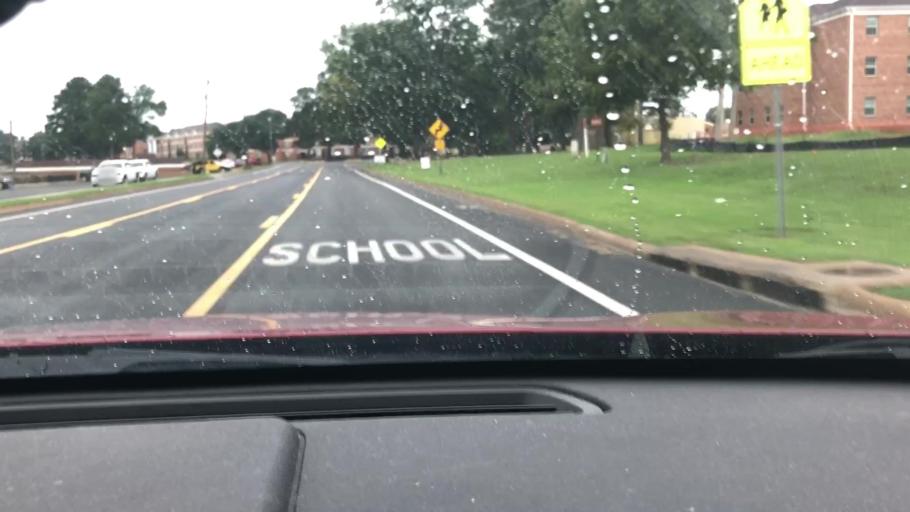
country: US
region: Arkansas
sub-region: Columbia County
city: Magnolia
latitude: 33.2952
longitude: -93.2373
